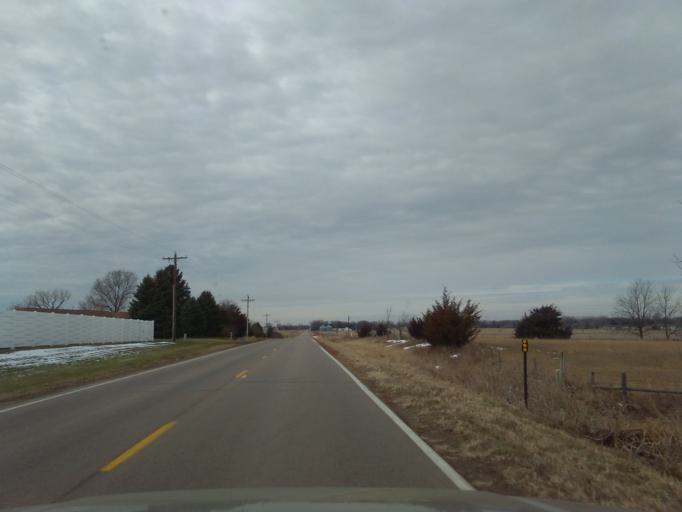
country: US
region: Nebraska
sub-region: Hall County
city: Grand Island
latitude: 40.7709
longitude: -98.3959
